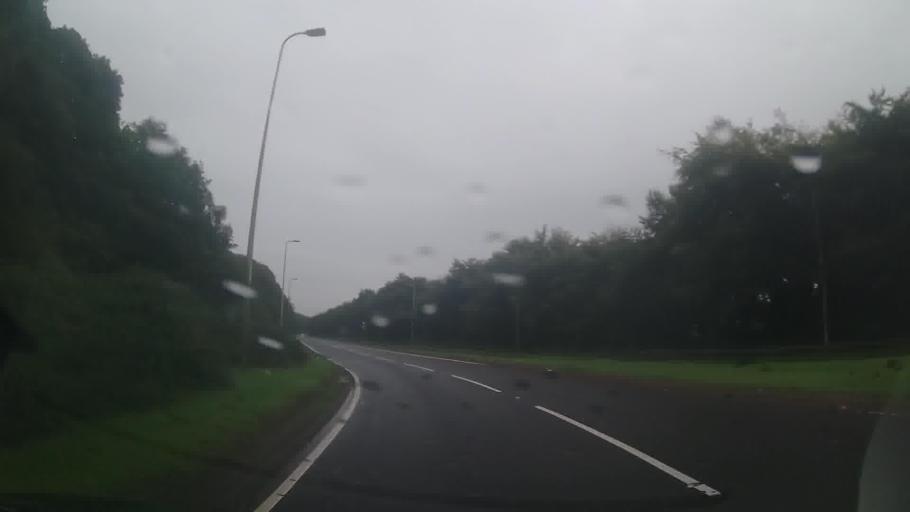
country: GB
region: Scotland
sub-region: North Ayrshire
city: Fairlie
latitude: 55.7278
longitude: -4.8655
